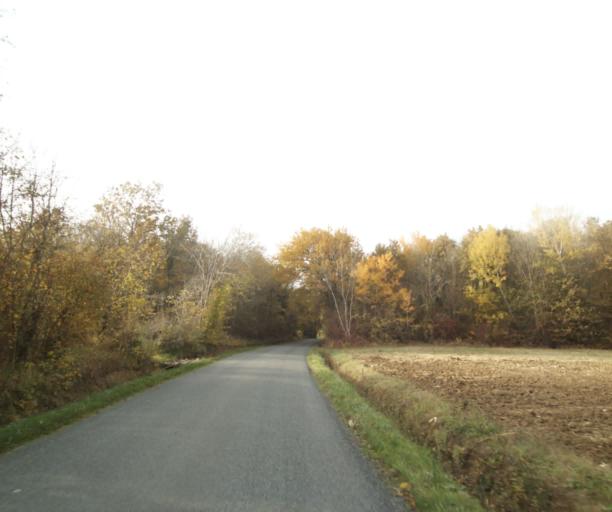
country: FR
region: Poitou-Charentes
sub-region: Departement de la Charente-Maritime
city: Nieul-les-Saintes
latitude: 45.7781
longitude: -0.7364
